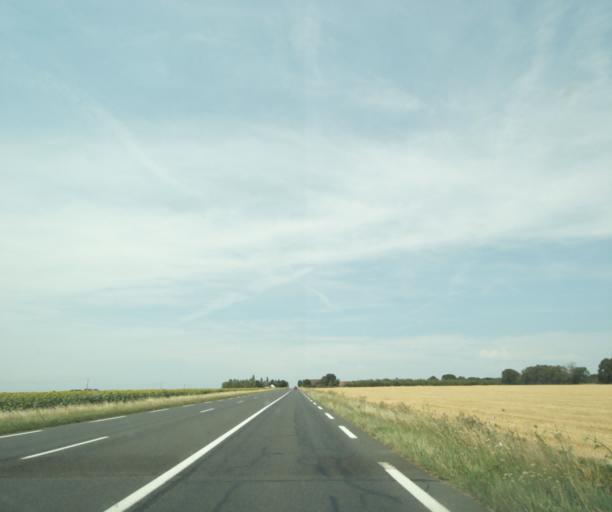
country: FR
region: Centre
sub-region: Departement d'Indre-et-Loire
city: Sainte-Maure-de-Touraine
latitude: 47.1681
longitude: 0.6523
